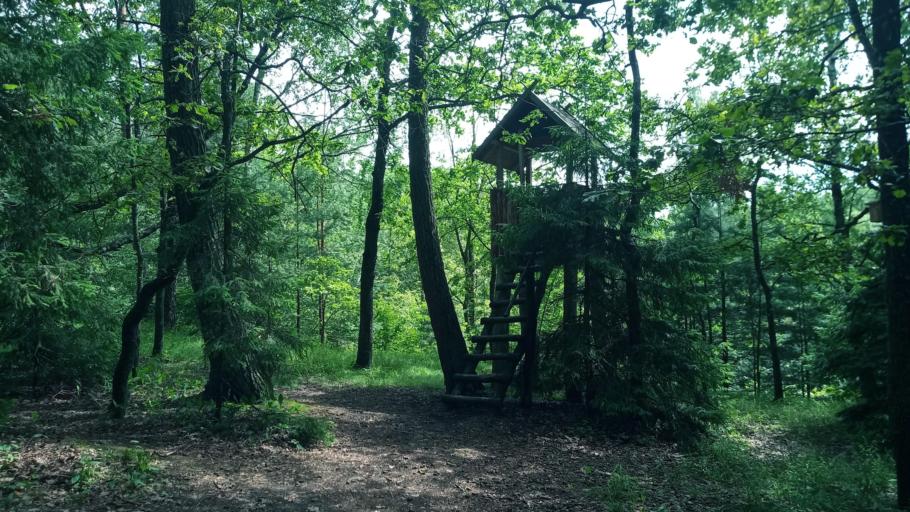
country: LT
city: Ramygala
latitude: 55.5320
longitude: 24.1160
